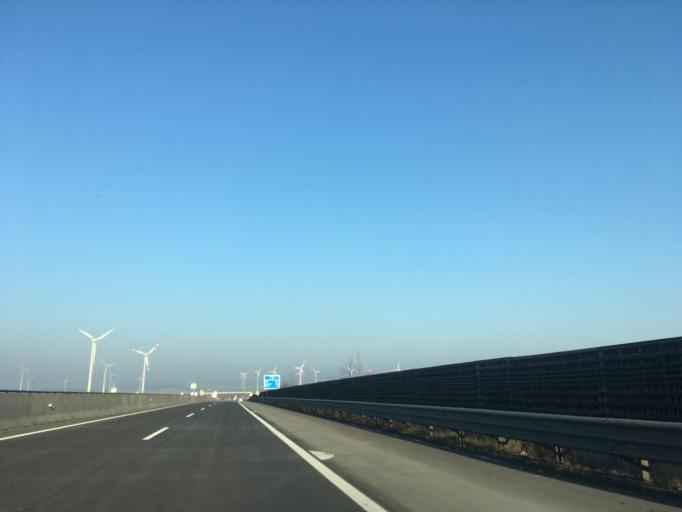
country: AT
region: Burgenland
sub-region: Politischer Bezirk Neusiedl am See
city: Kittsee
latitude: 48.0738
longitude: 17.0635
